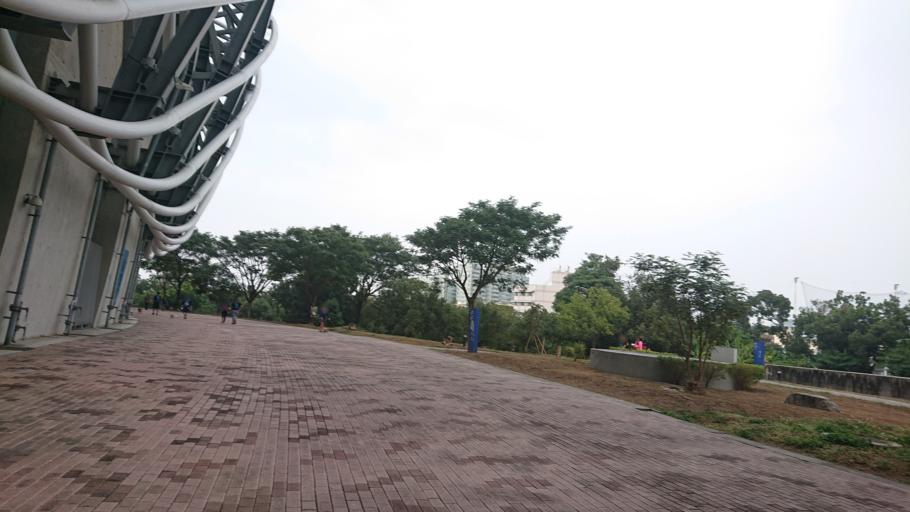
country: TW
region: Kaohsiung
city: Kaohsiung
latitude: 22.7041
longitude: 120.2952
